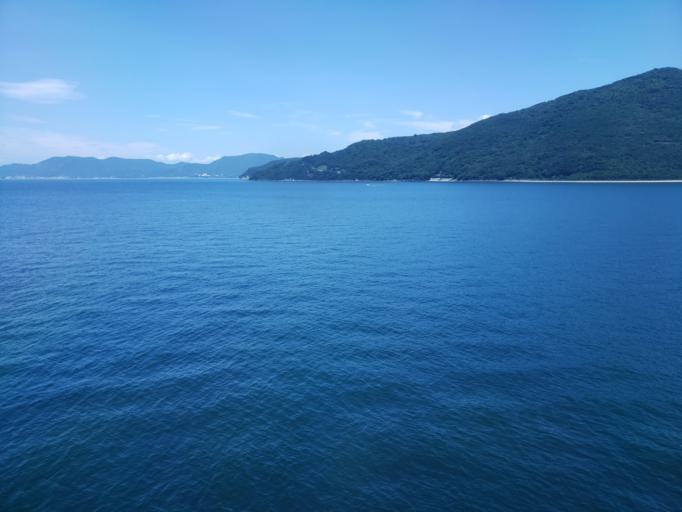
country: JP
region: Kagawa
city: Tonosho
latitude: 34.4070
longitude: 134.2251
